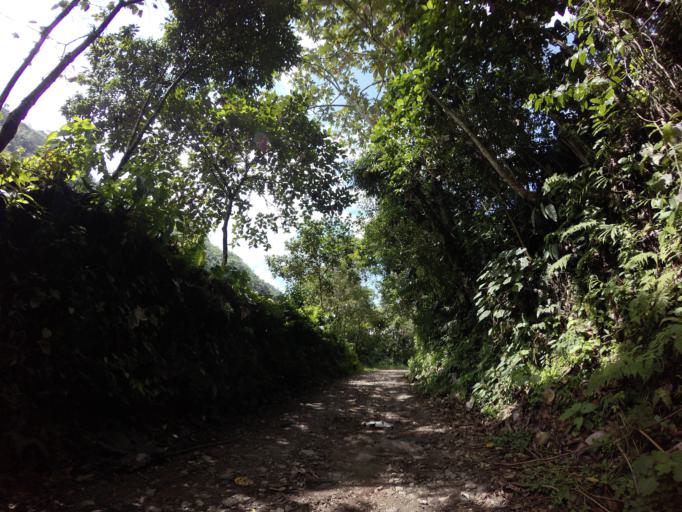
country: CO
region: Antioquia
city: Narino
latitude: 5.5252
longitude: -75.1754
